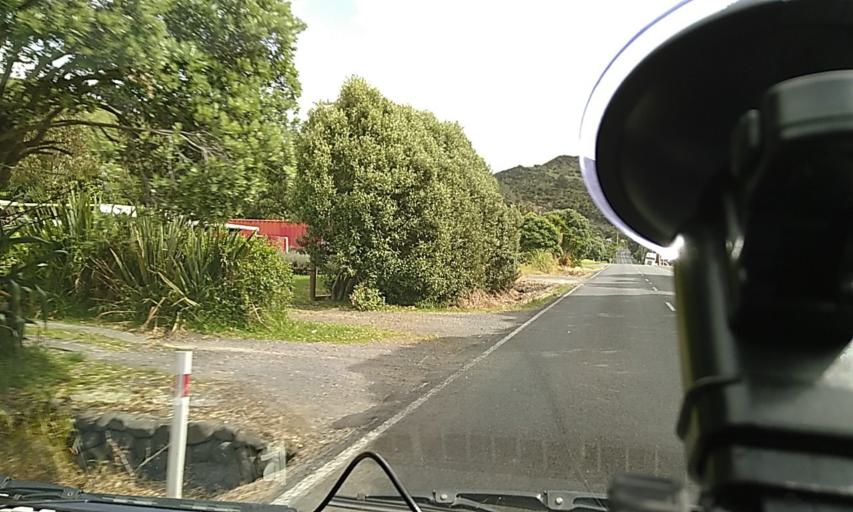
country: NZ
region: Northland
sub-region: Far North District
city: Ahipara
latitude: -35.5335
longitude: 173.3888
